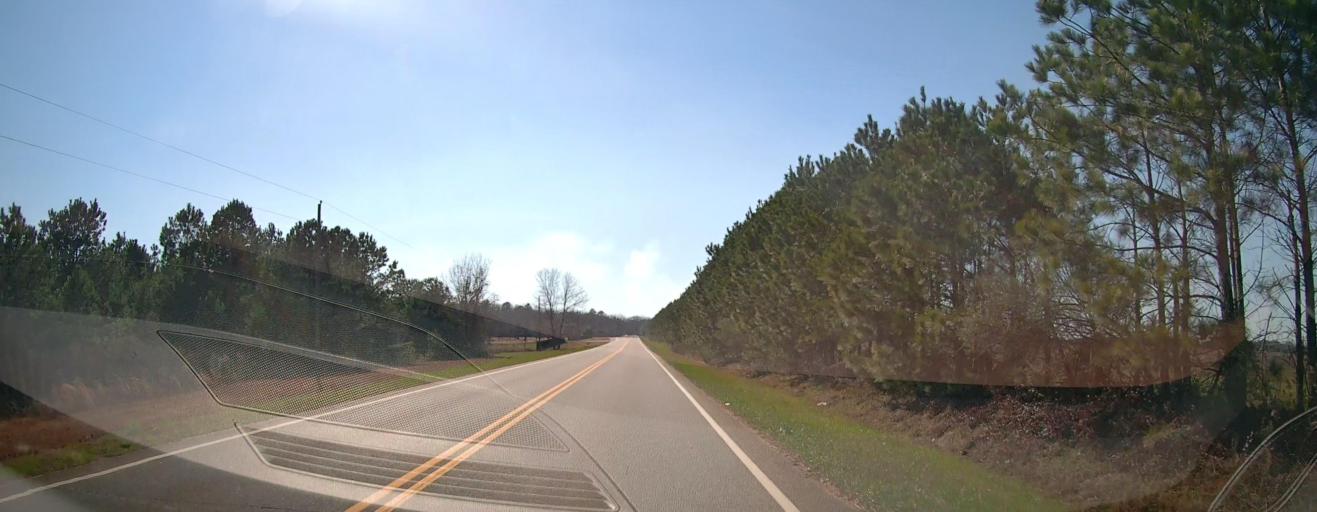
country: US
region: Georgia
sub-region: Macon County
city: Oglethorpe
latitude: 32.2086
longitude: -84.1241
